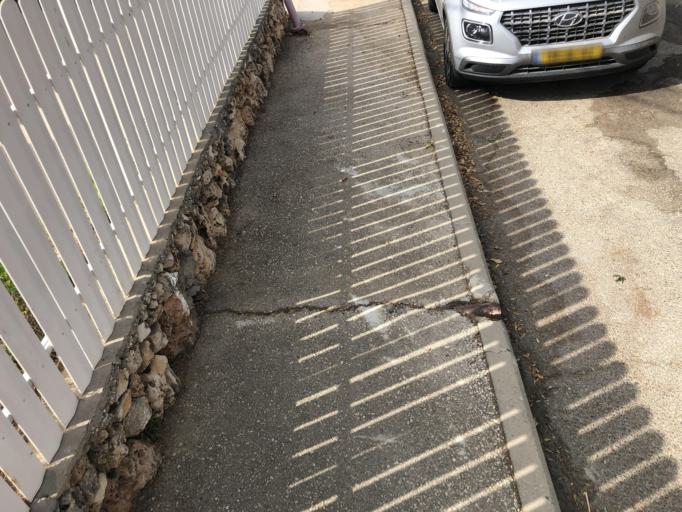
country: PS
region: West Bank
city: Jit
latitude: 32.2115
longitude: 35.1602
